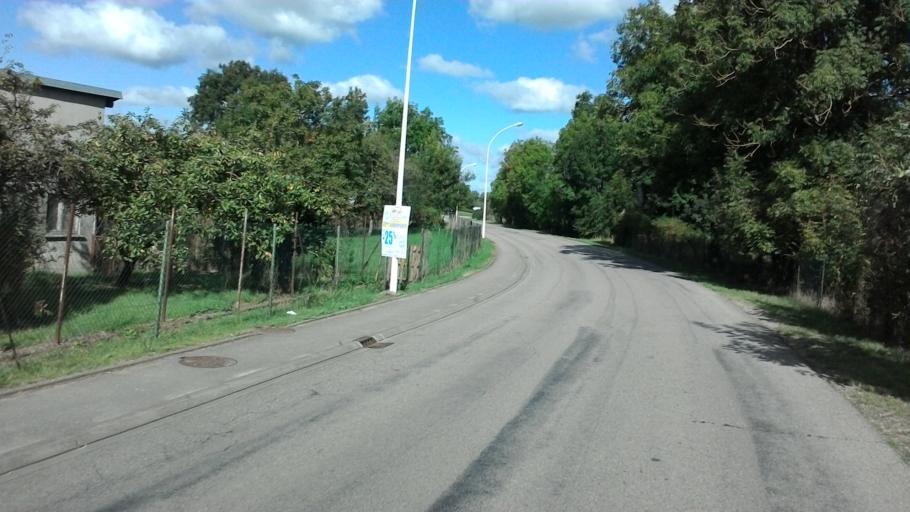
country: FR
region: Lorraine
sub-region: Departement des Vosges
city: Neufchateau
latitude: 48.3598
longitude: 5.6829
